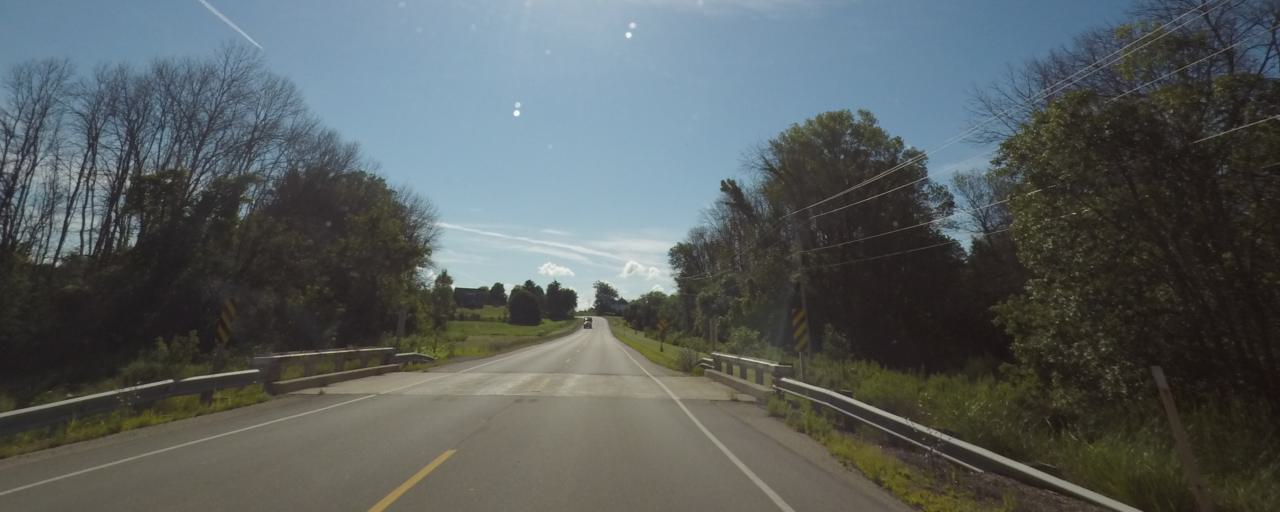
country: US
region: Wisconsin
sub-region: Jefferson County
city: Johnson Creek
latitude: 43.0721
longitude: -88.7022
